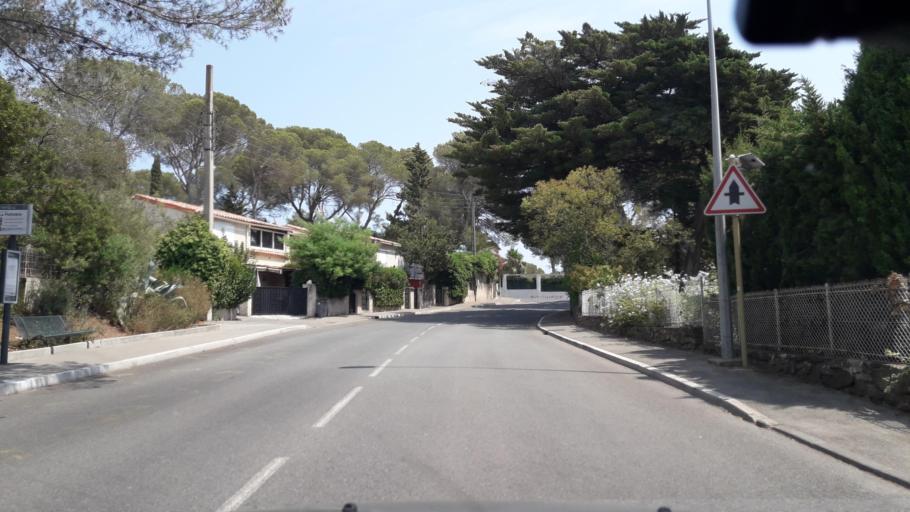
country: FR
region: Provence-Alpes-Cote d'Azur
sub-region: Departement du Var
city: Saint-Raphael
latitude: 43.4194
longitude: 6.8061
